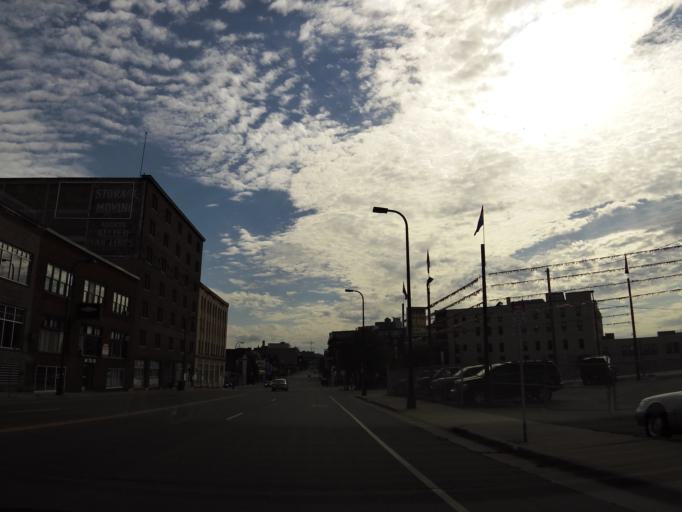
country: US
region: Minnesota
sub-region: Hennepin County
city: Minneapolis
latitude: 44.9917
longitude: -93.2511
